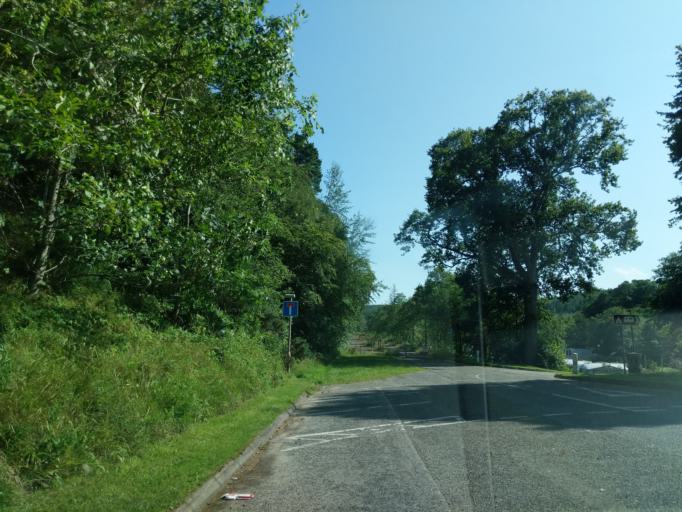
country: GB
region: Scotland
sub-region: Moray
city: Fochabers
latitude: 57.6092
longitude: -3.0885
